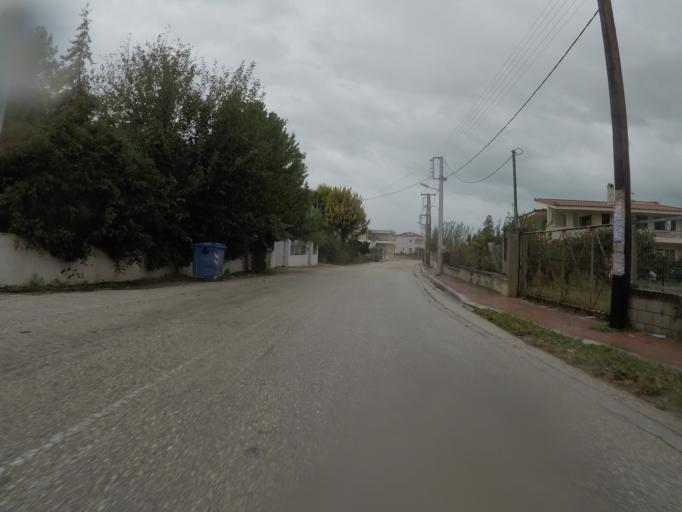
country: GR
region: Peloponnese
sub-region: Nomos Korinthias
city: Arkhaia Korinthos
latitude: 37.9055
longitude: 22.8842
